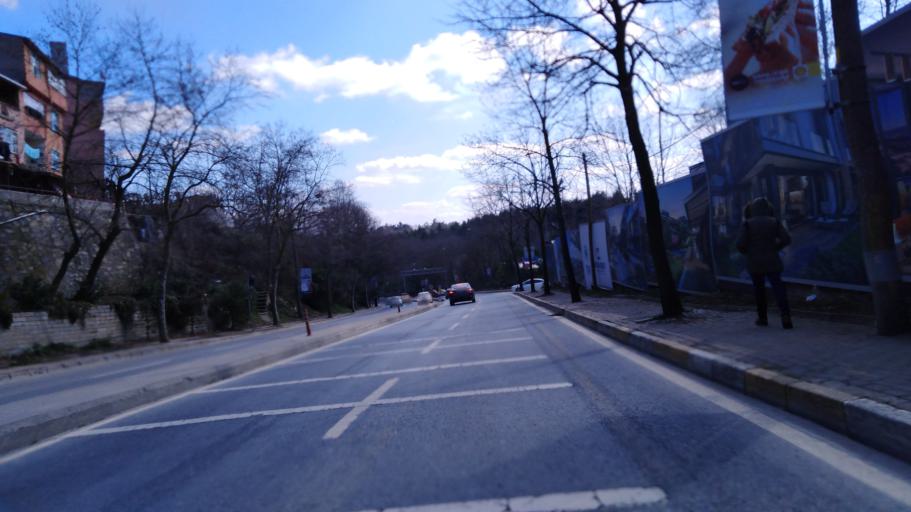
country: TR
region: Istanbul
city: Sisli
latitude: 41.1115
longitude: 29.0463
